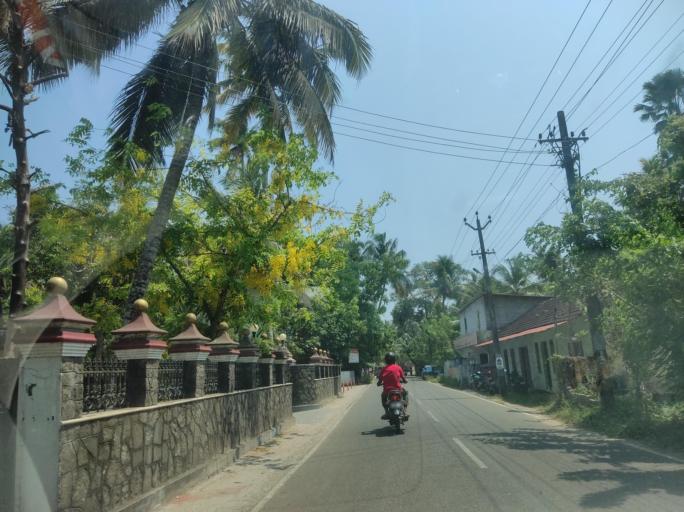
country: IN
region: Kerala
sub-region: Alappuzha
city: Kutiatodu
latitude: 9.7850
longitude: 76.3040
